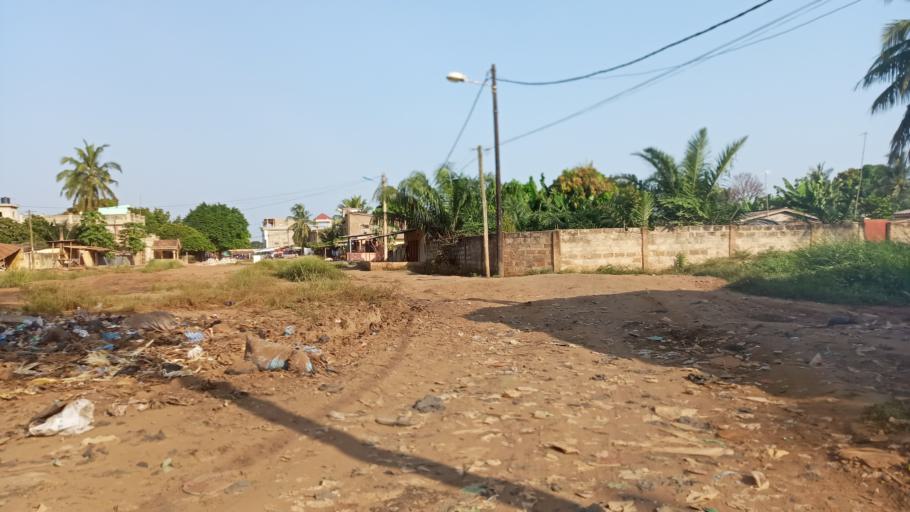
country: TG
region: Maritime
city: Lome
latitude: 6.1804
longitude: 1.1610
